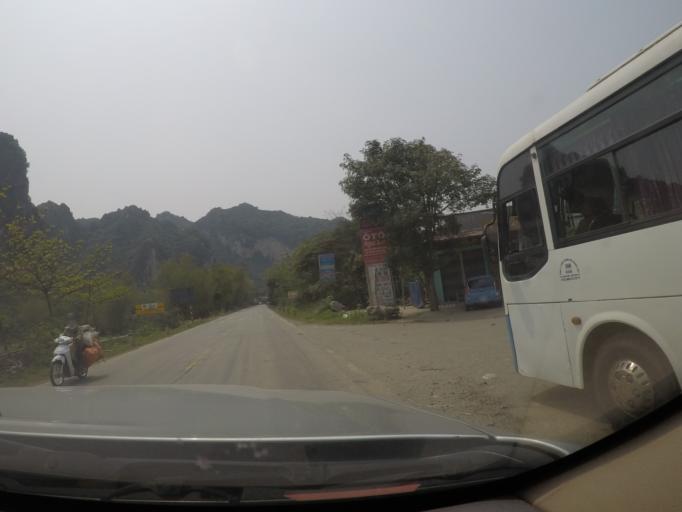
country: VN
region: Thanh Hoa
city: Thi Tran Cam Thuy
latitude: 20.2222
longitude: 105.4916
